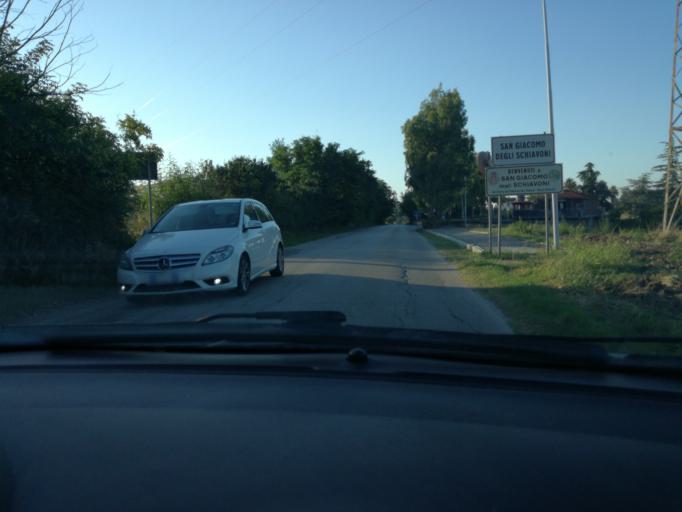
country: IT
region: Molise
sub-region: Provincia di Campobasso
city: San Giacomo degli Schiavoni
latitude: 41.9586
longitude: 14.9443
